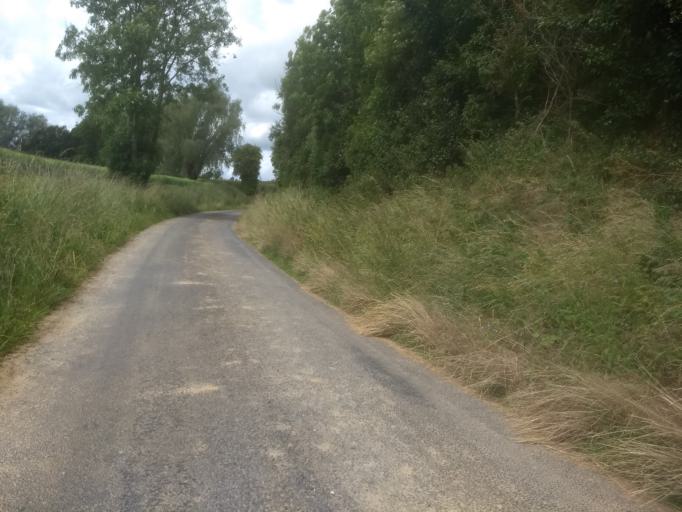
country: FR
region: Nord-Pas-de-Calais
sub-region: Departement du Pas-de-Calais
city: Beaumetz-les-Loges
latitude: 50.2264
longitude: 2.6406
